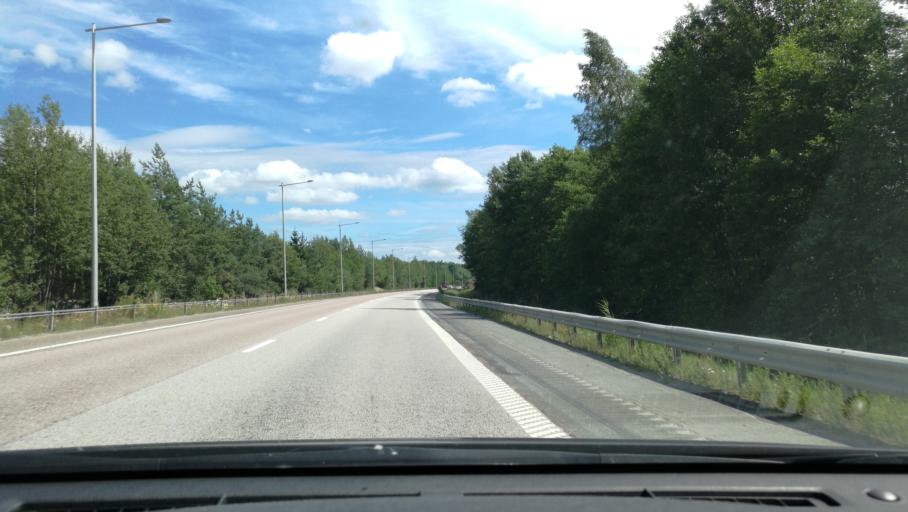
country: SE
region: Stockholm
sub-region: Upplands-Bro Kommun
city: Bro
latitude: 59.5233
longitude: 17.6560
